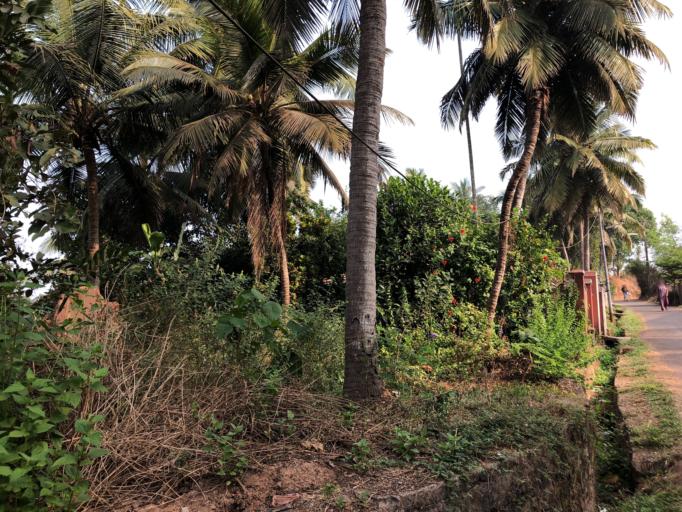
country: IN
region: Karnataka
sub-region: Dakshina Kannada
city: Mangalore
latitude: 12.8723
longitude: 74.8941
